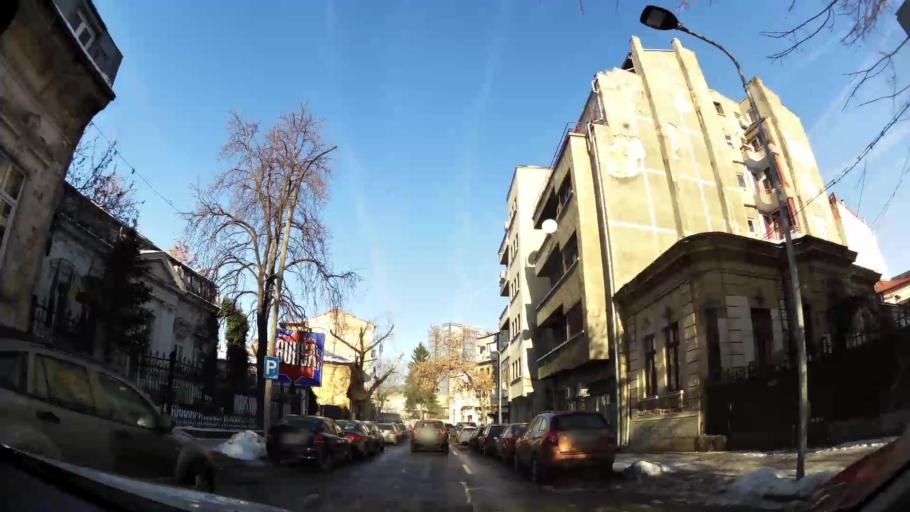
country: RO
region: Bucuresti
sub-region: Municipiul Bucuresti
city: Bucuresti
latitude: 44.4441
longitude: 26.0829
